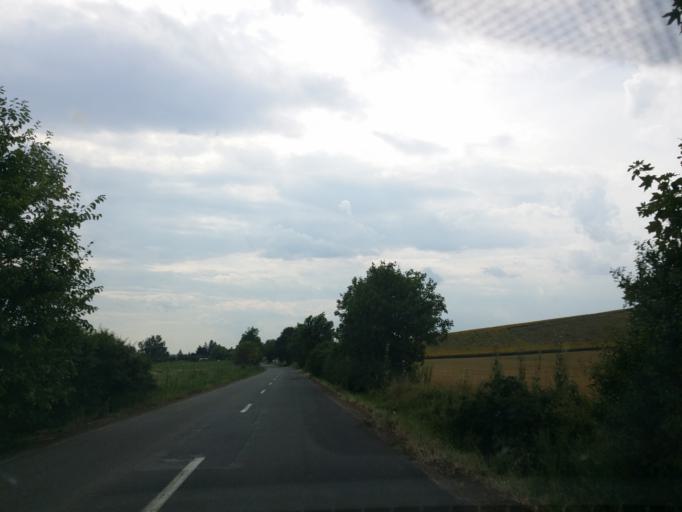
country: HU
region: Nograd
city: Bercel
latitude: 47.9796
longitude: 19.3894
